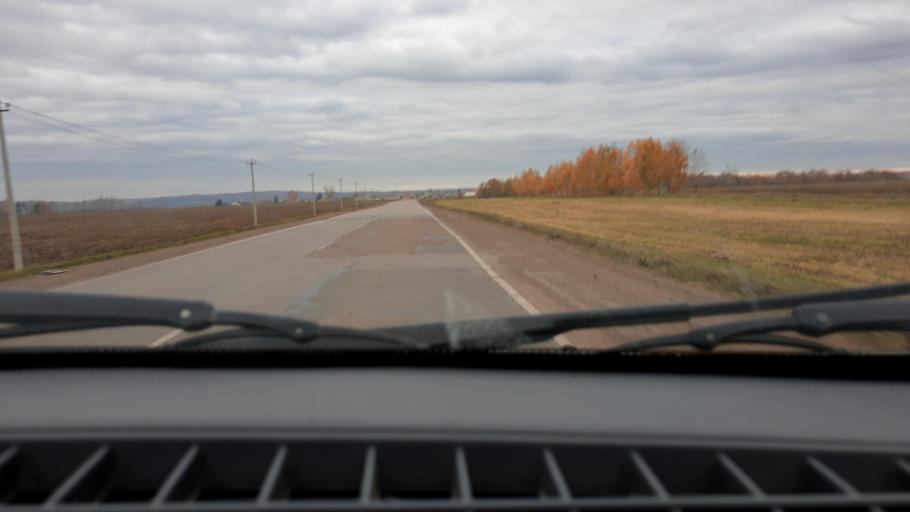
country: RU
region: Bashkortostan
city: Kabakovo
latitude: 54.5435
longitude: 56.0801
